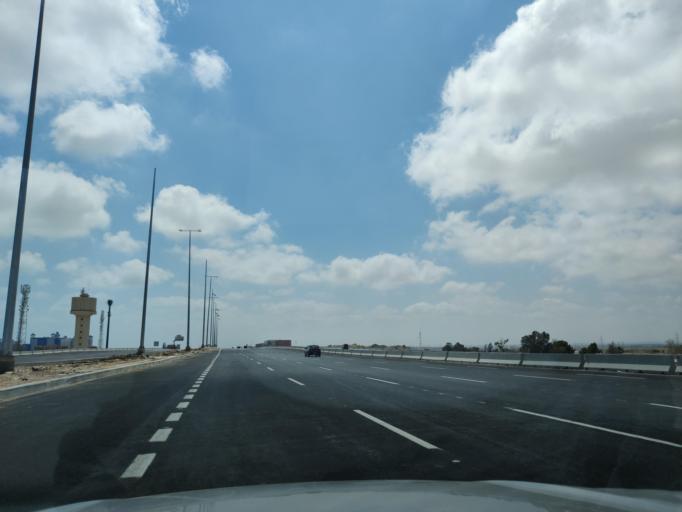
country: EG
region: Muhafazat Matruh
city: Al `Alamayn
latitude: 30.8229
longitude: 28.9909
